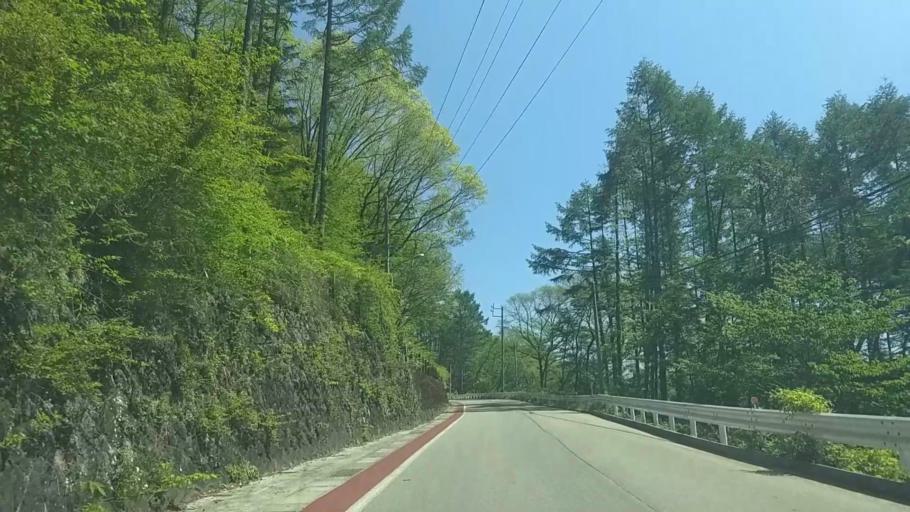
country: JP
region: Yamanashi
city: Nirasaki
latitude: 35.9204
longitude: 138.4459
